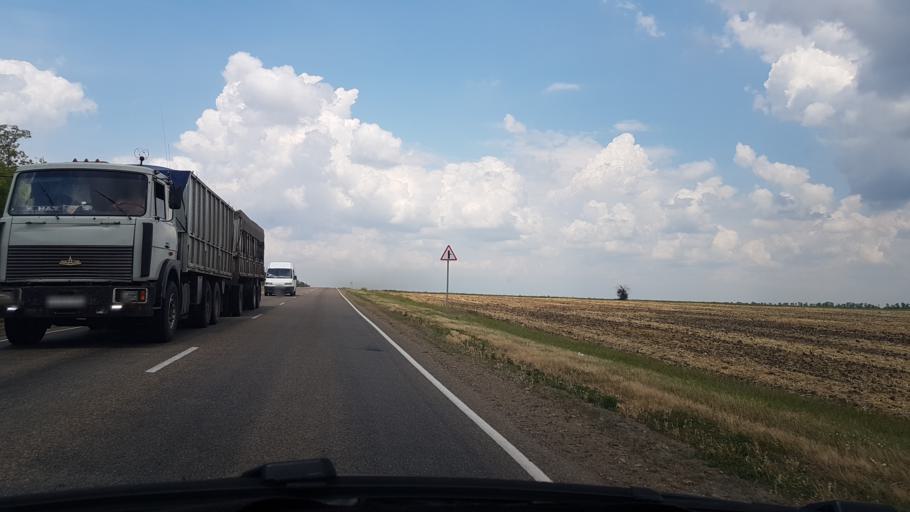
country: RU
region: Krasnodarskiy
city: Dmitriyevskaya
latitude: 45.6776
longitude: 40.7440
